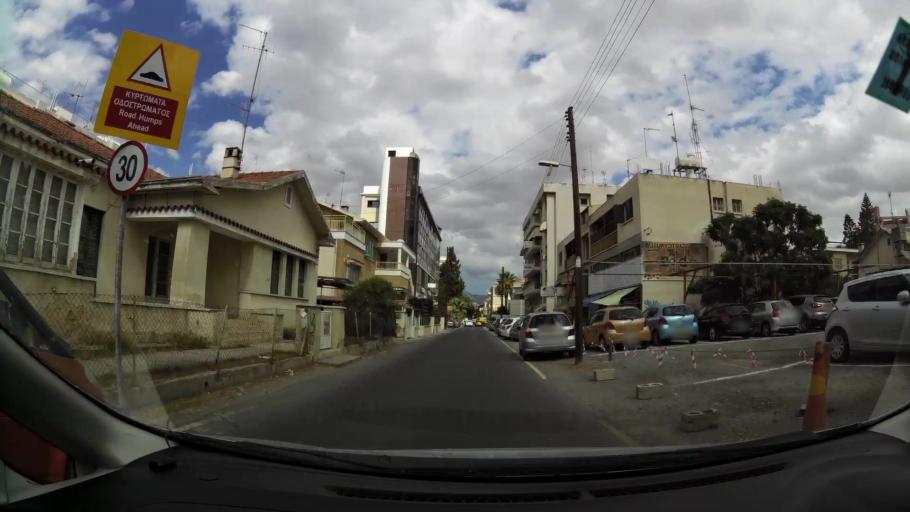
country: CY
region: Lefkosia
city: Nicosia
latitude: 35.1659
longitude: 33.3647
